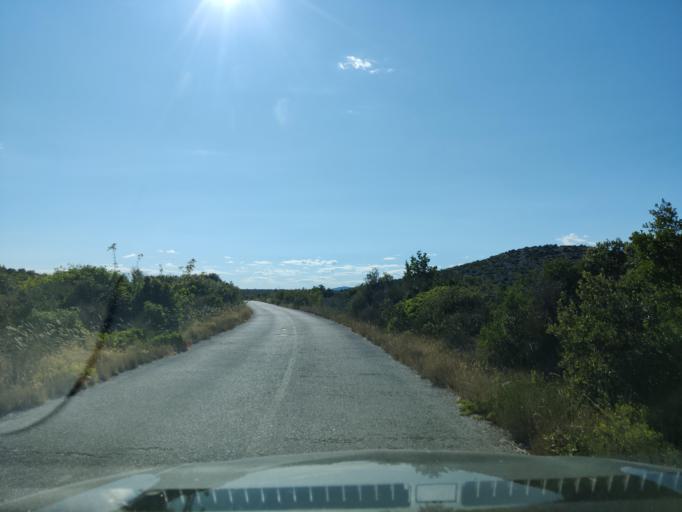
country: HR
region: Sibensko-Kniniska
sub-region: Grad Sibenik
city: Sibenik
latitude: 43.7393
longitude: 15.8697
